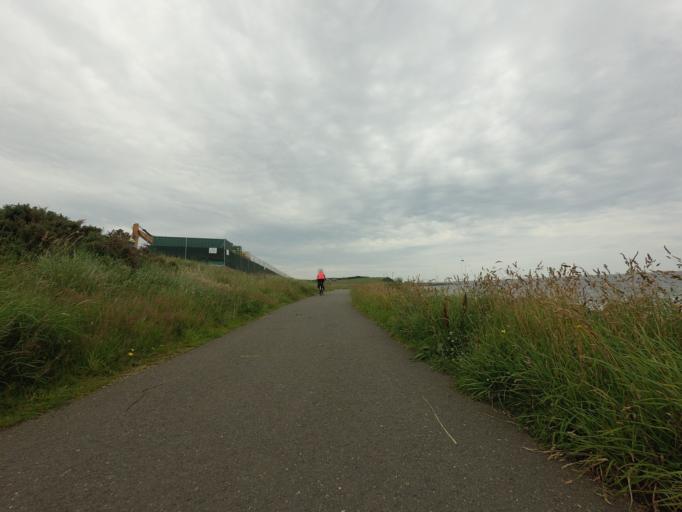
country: GB
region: Scotland
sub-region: Aberdeenshire
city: Whitehills
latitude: 57.6735
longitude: -2.5643
